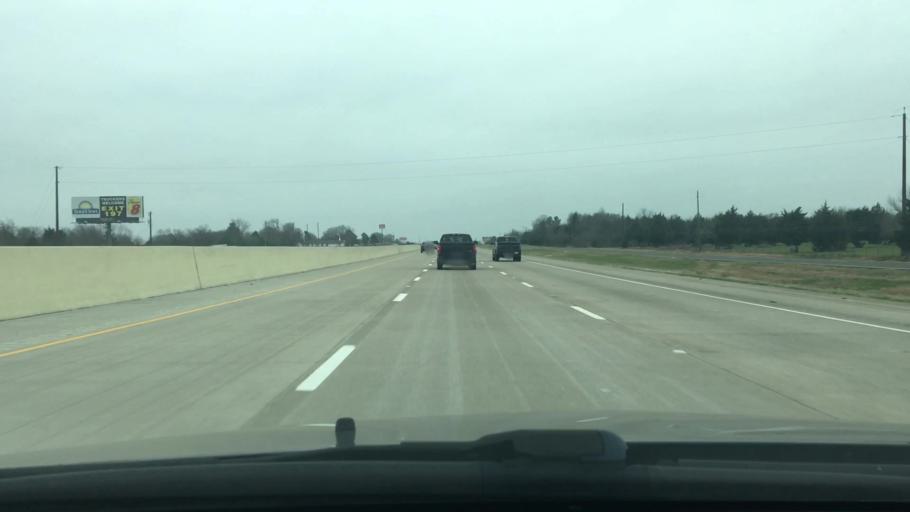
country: US
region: Texas
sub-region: Navarro County
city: Corsicana
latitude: 31.9976
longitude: -96.4294
